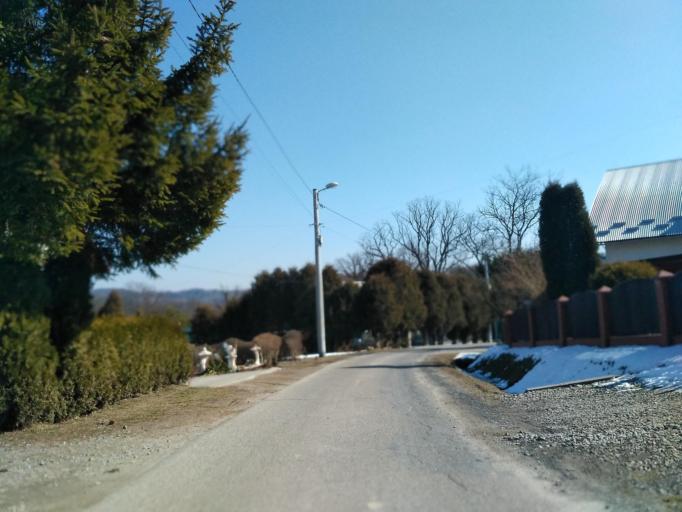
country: PL
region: Subcarpathian Voivodeship
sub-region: Powiat brzozowski
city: Jasienica Rosielna
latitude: 49.7553
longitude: 21.9457
